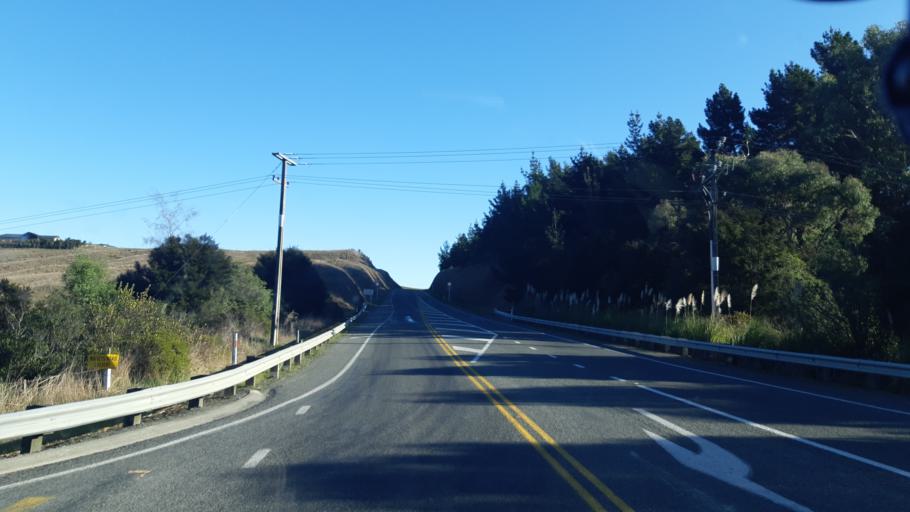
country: NZ
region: Tasman
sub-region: Tasman District
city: Mapua
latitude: -41.2890
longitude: 173.0873
